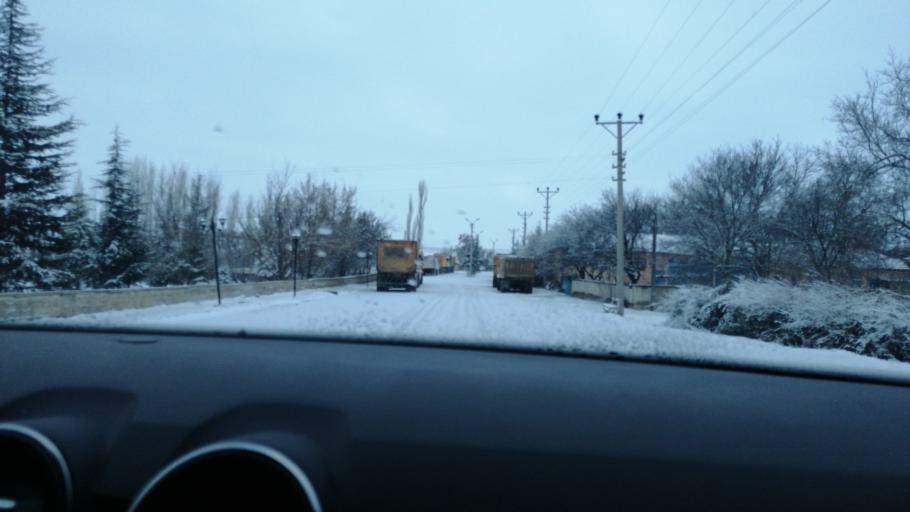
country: TR
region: Aksaray
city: Agacoren
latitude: 38.9316
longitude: 33.9490
